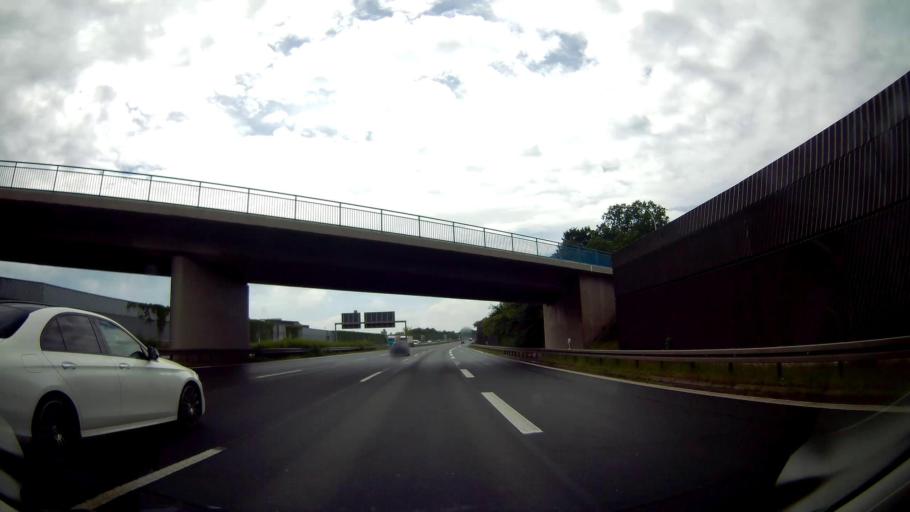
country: DE
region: North Rhine-Westphalia
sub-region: Regierungsbezirk Detmold
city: Rheda-Wiedenbruck
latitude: 51.8517
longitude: 8.3168
